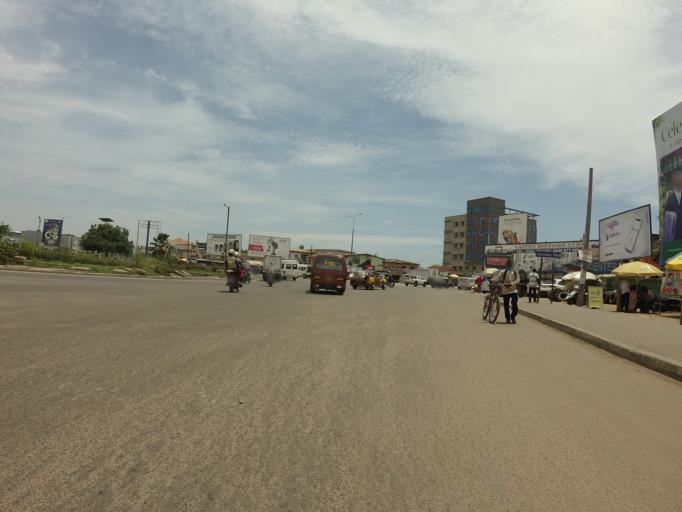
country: GH
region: Greater Accra
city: Accra
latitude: 5.5614
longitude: -0.2298
